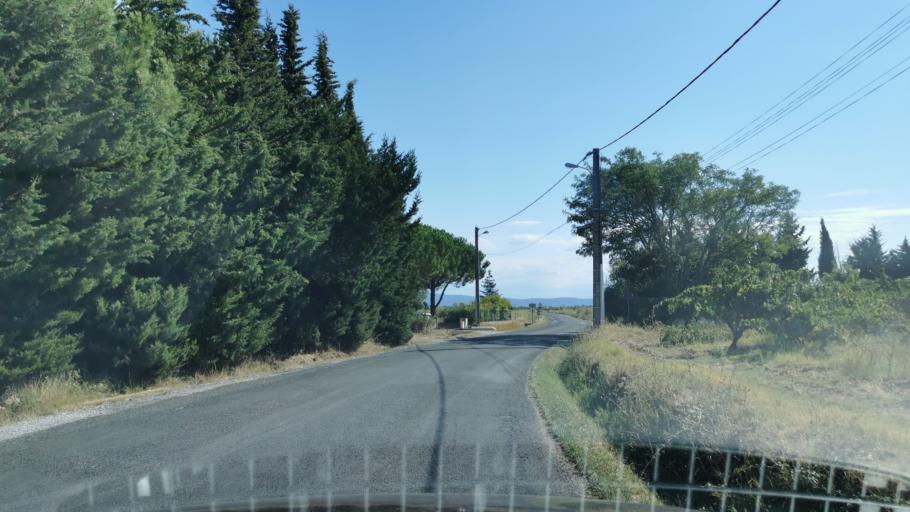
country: FR
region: Languedoc-Roussillon
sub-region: Departement de l'Aude
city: Peyriac-Minervois
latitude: 43.3102
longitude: 2.5633
